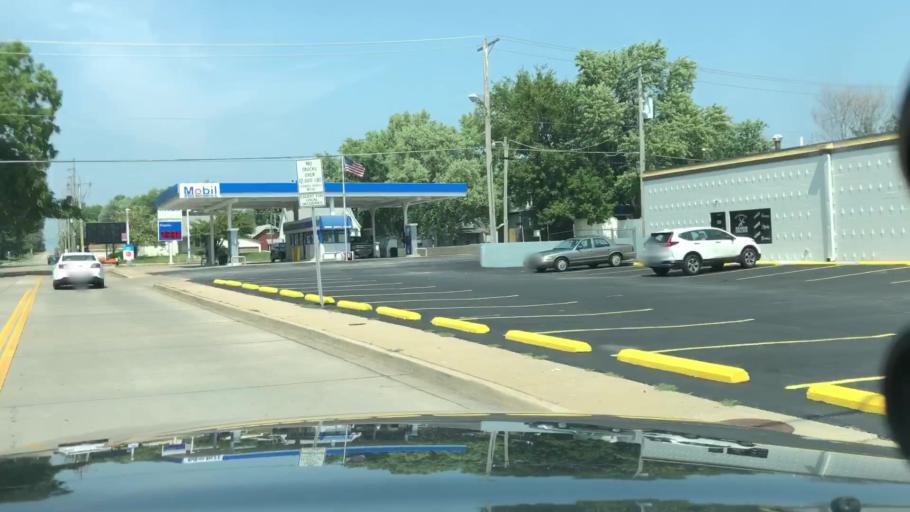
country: US
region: Missouri
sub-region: Saint Charles County
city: Saint Charles
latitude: 38.7873
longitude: -90.4932
